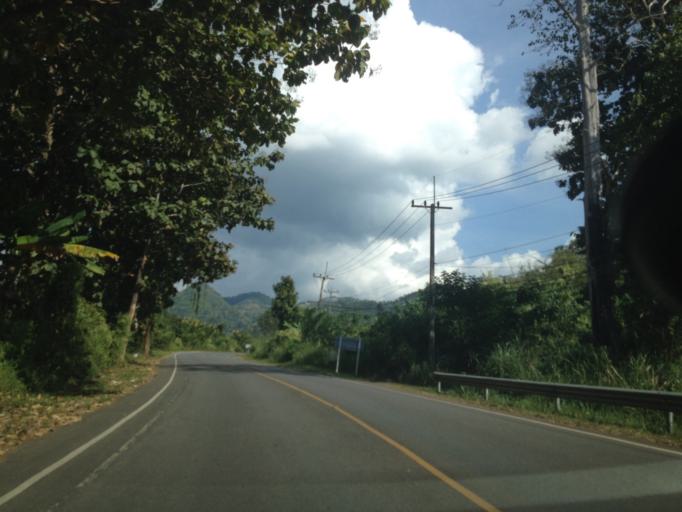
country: TH
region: Chiang Mai
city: Samoeng
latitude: 18.8523
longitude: 98.7535
